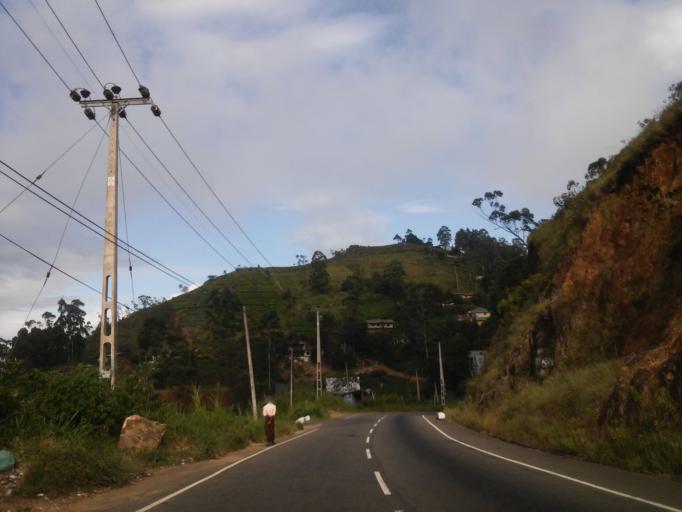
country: LK
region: Uva
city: Haputale
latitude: 6.7654
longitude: 80.9549
